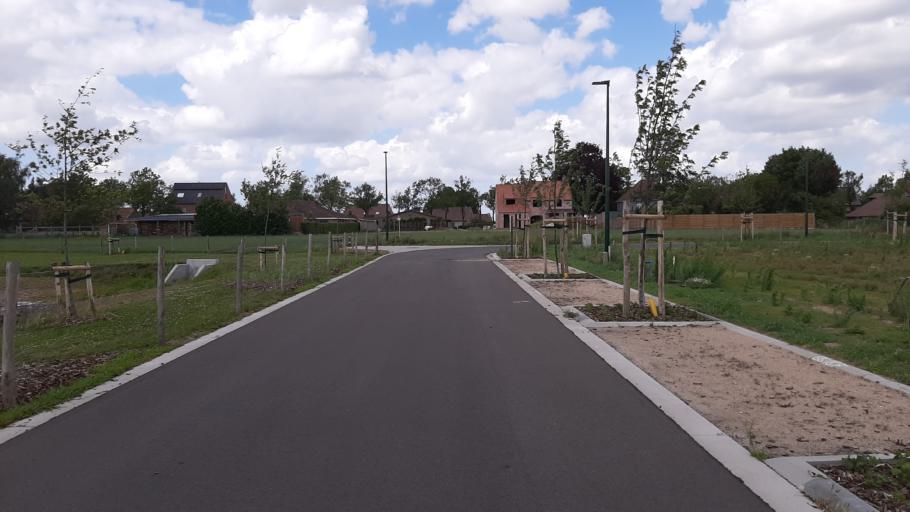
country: BE
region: Flanders
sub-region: Provincie Oost-Vlaanderen
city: Kaprijke
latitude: 51.2165
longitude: 3.6080
